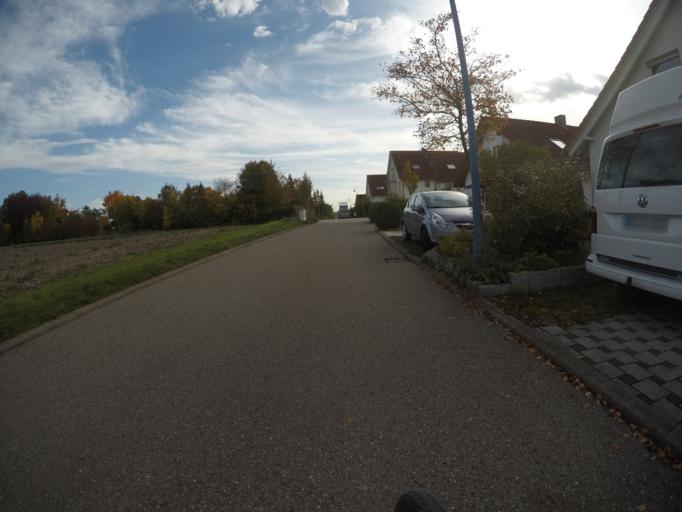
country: DE
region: Baden-Wuerttemberg
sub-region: Regierungsbezirk Stuttgart
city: Herrenberg
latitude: 48.5812
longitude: 8.8792
